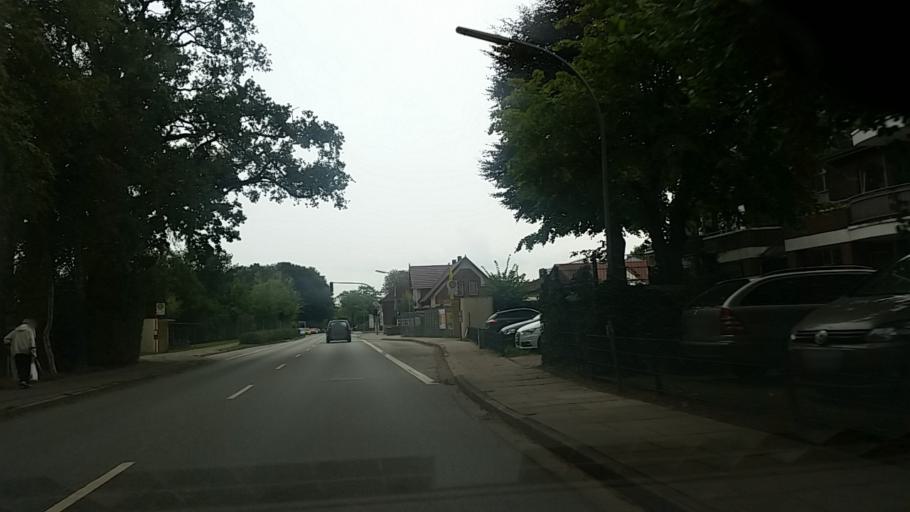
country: DE
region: Schleswig-Holstein
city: Nahe
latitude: 53.7920
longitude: 10.1381
